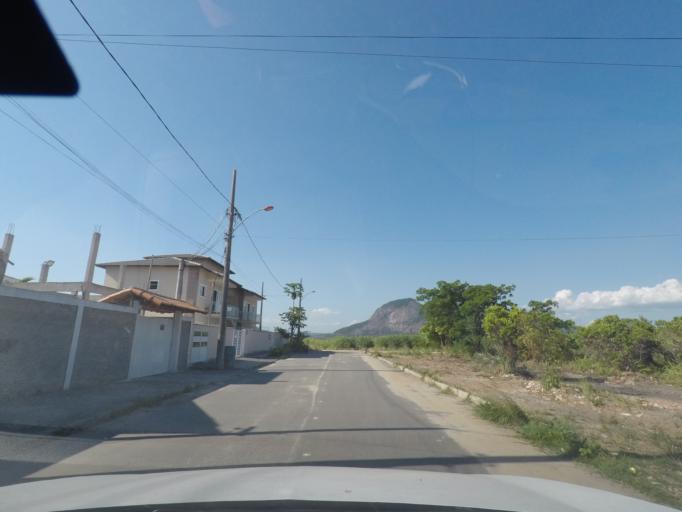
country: BR
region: Rio de Janeiro
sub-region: Marica
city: Marica
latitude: -22.9656
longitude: -42.9200
